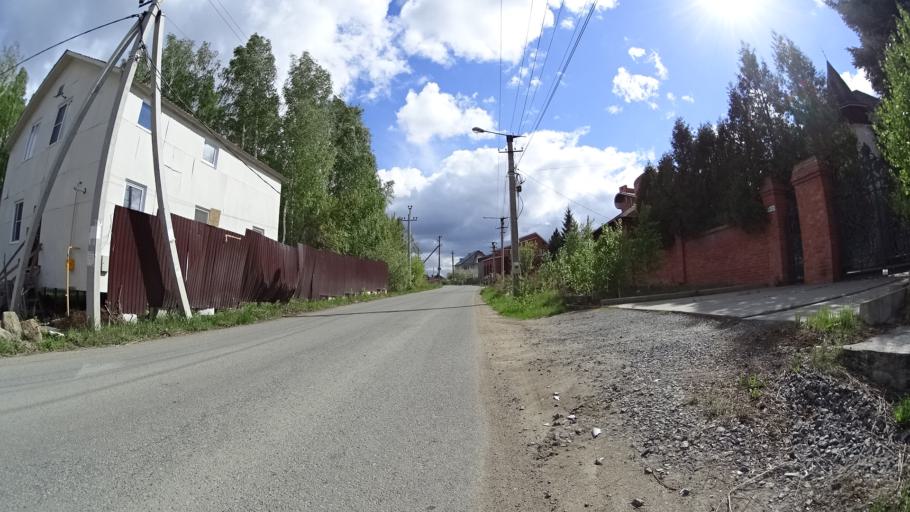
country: RU
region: Chelyabinsk
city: Sargazy
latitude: 55.1505
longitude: 61.2379
